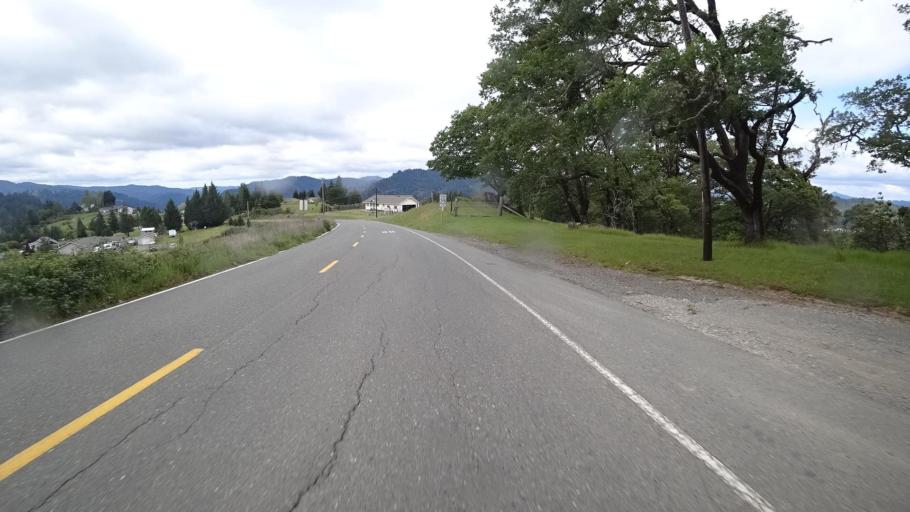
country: US
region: California
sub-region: Humboldt County
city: Redway
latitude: 40.1112
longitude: -123.7835
